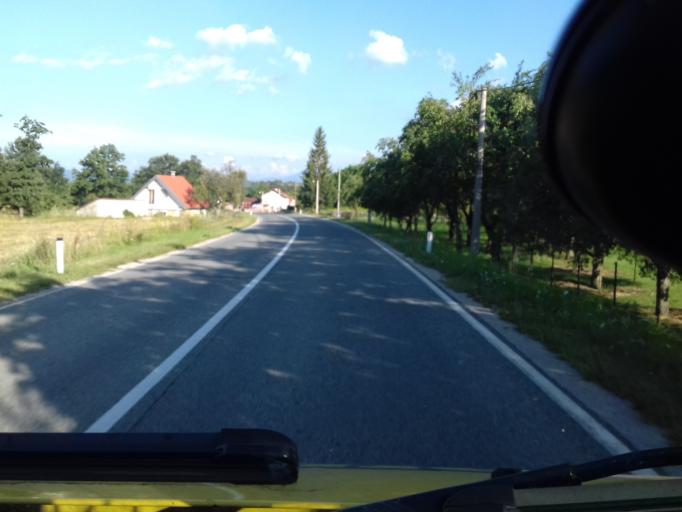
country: BA
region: Federation of Bosnia and Herzegovina
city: Orasac
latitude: 44.6373
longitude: 16.1743
